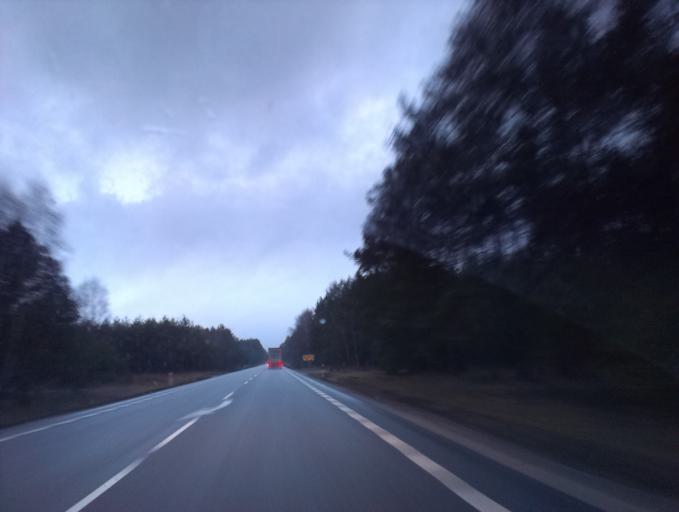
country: PL
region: Swietokrzyskie
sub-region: Powiat konecki
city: Ruda Maleniecka
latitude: 51.1888
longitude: 20.2148
